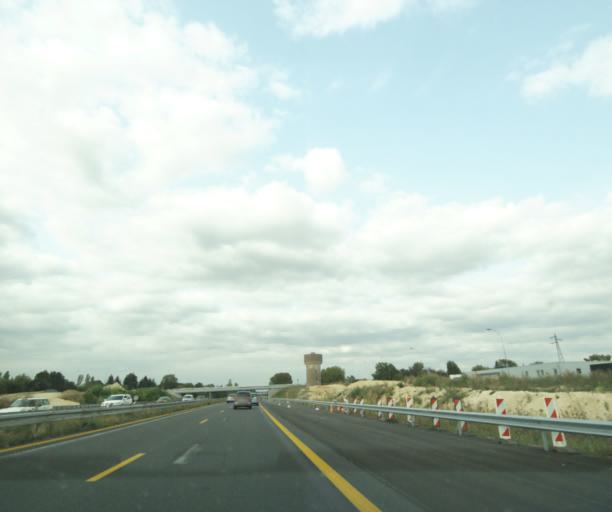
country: FR
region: Centre
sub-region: Departement d'Indre-et-Loire
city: Chambray-les-Tours
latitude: 47.3418
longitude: 0.6989
